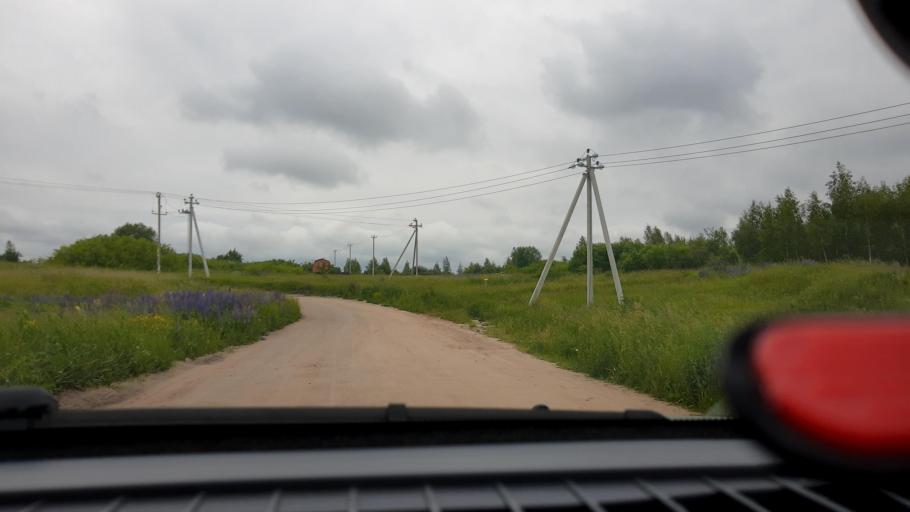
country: RU
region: Nizjnij Novgorod
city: Burevestnik
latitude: 56.1029
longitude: 43.9473
